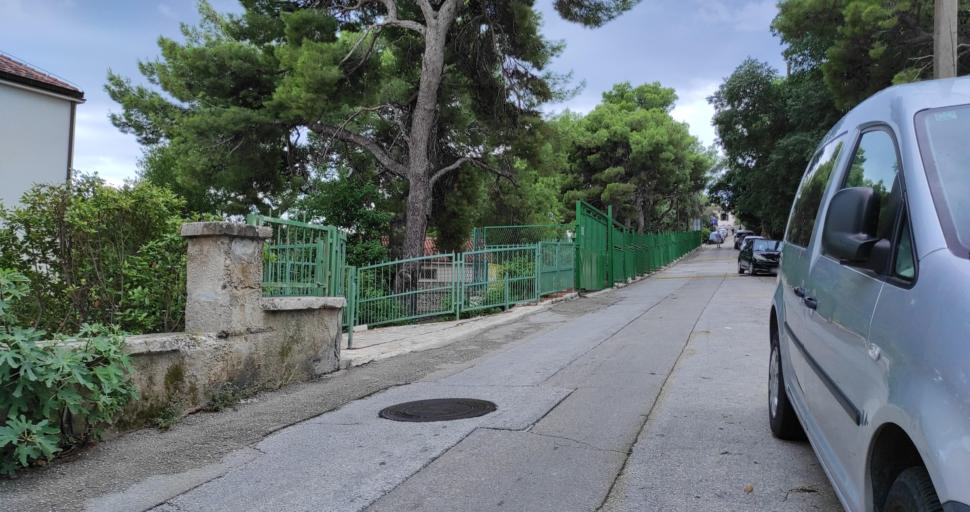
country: HR
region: Splitsko-Dalmatinska
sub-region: Grad Split
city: Split
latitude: 43.5095
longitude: 16.4309
